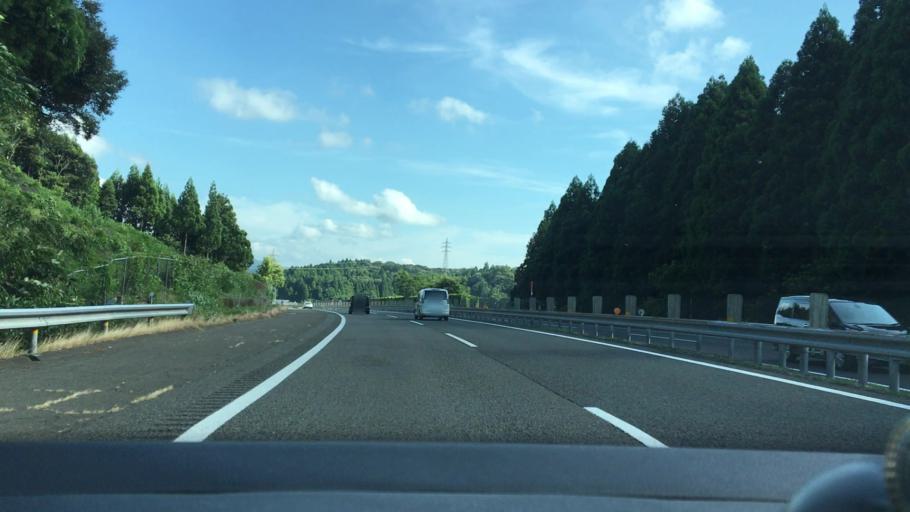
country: JP
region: Fukui
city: Maruoka
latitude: 36.2567
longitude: 136.2827
